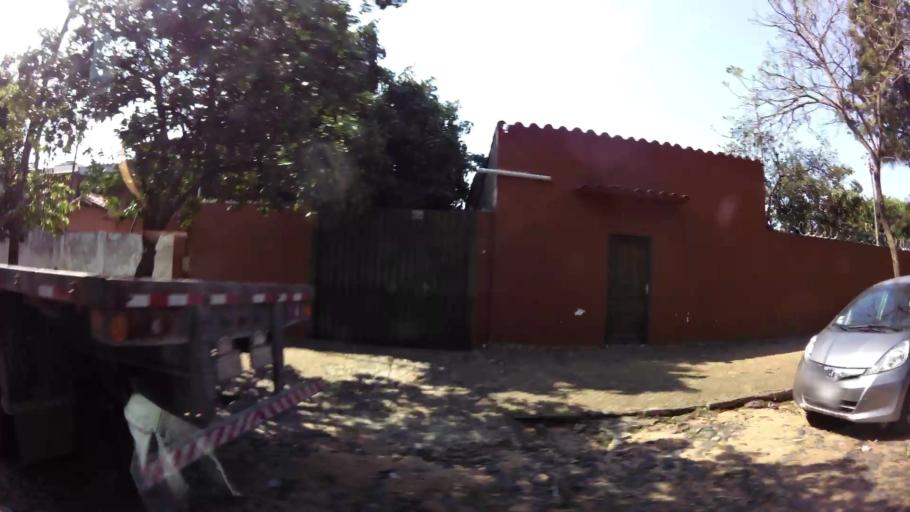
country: PY
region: Asuncion
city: Asuncion
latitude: -25.3164
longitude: -57.6310
